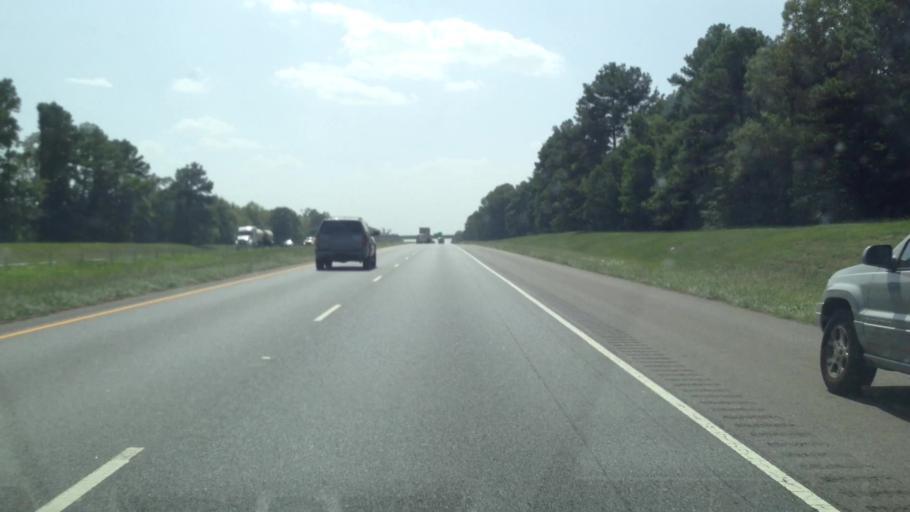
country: US
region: Louisiana
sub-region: Bossier Parish
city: Red Chute
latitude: 32.5421
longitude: -93.5955
